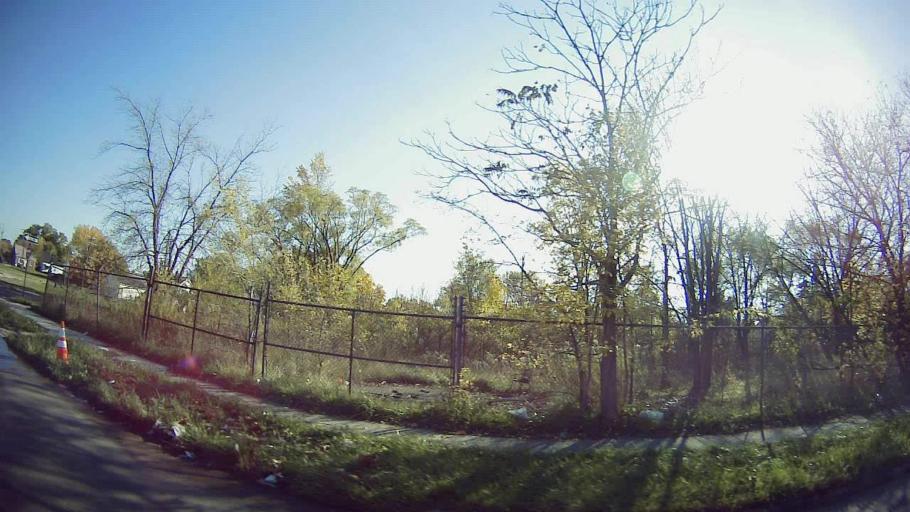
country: US
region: Michigan
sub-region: Macomb County
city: Warren
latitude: 42.4338
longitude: -83.0320
